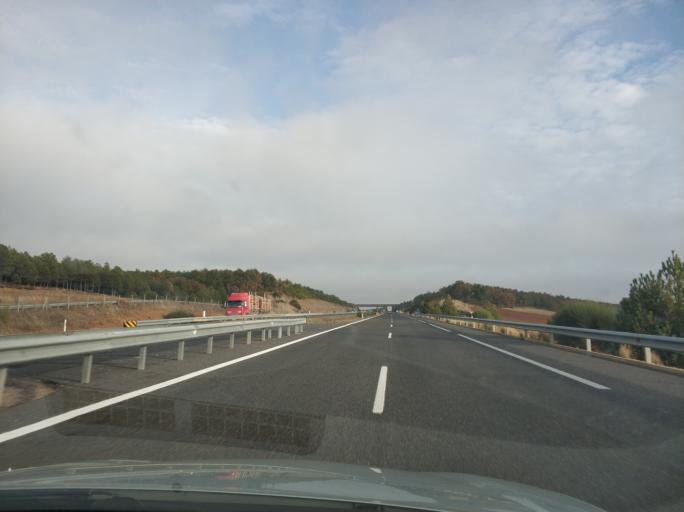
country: ES
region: Castille and Leon
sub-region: Provincia de Palencia
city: Ledigos
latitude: 42.3630
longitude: -4.8509
